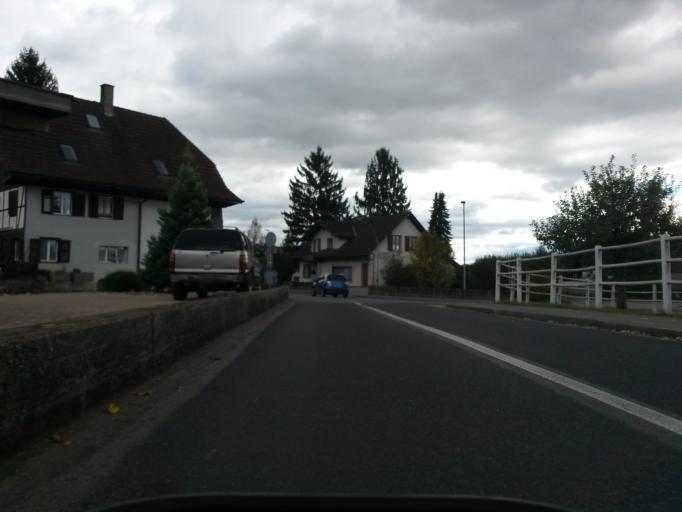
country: CH
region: Bern
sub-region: Biel/Bienne District
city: Orpund
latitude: 47.1347
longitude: 7.3144
